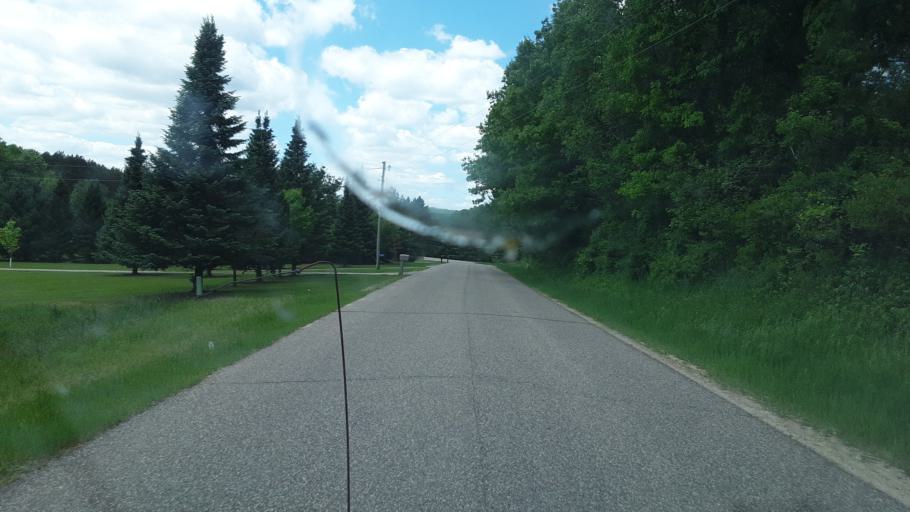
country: US
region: Wisconsin
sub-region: Sauk County
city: Reedsburg
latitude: 43.5617
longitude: -89.9901
